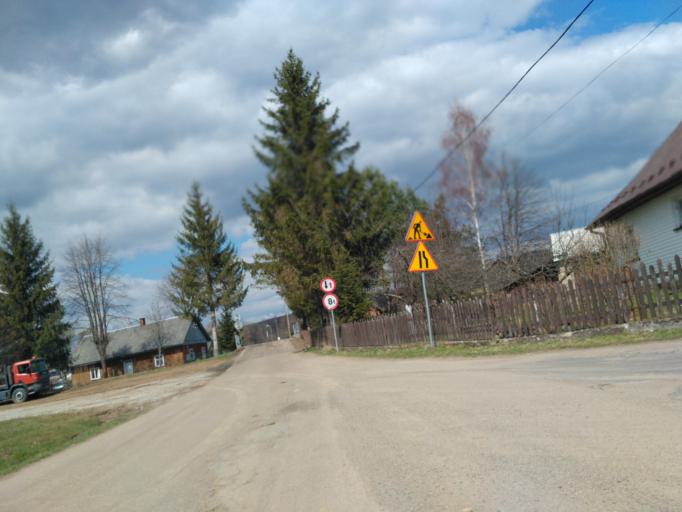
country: PL
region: Subcarpathian Voivodeship
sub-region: Powiat sanocki
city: Tyrawa Woloska
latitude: 49.6458
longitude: 22.2987
